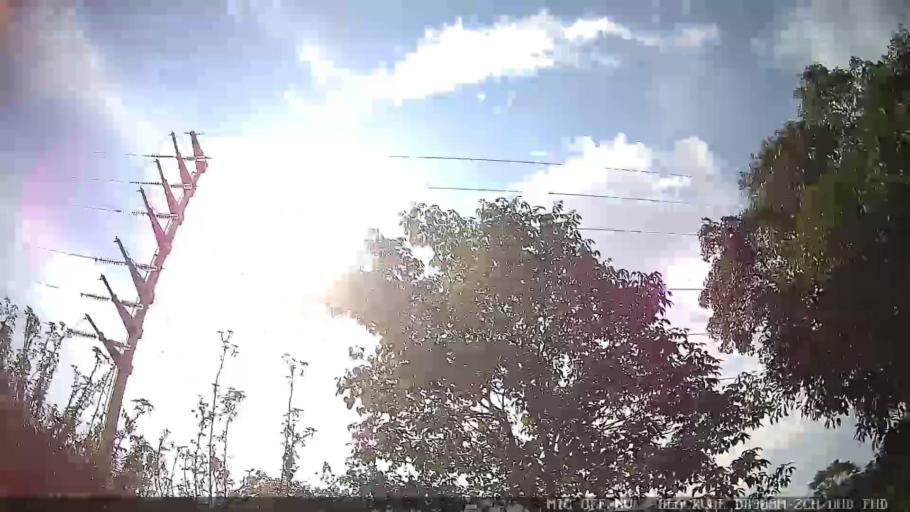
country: BR
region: Sao Paulo
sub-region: Braganca Paulista
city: Braganca Paulista
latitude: -22.9325
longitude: -46.5565
